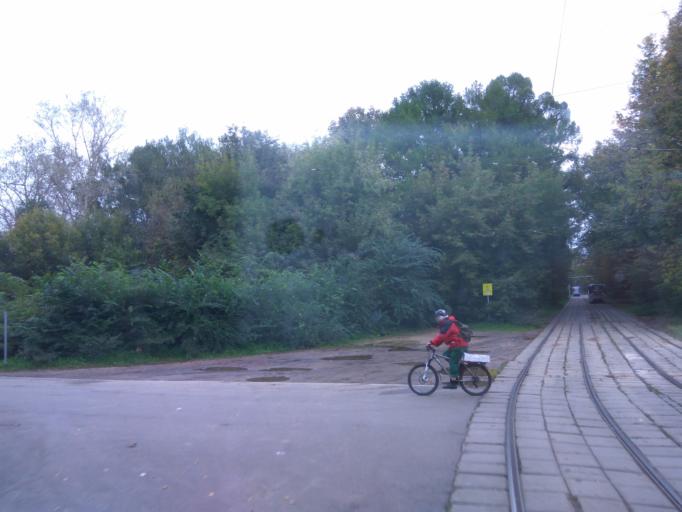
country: RU
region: Moskovskaya
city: Bogorodskoye
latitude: 55.7865
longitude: 37.7476
